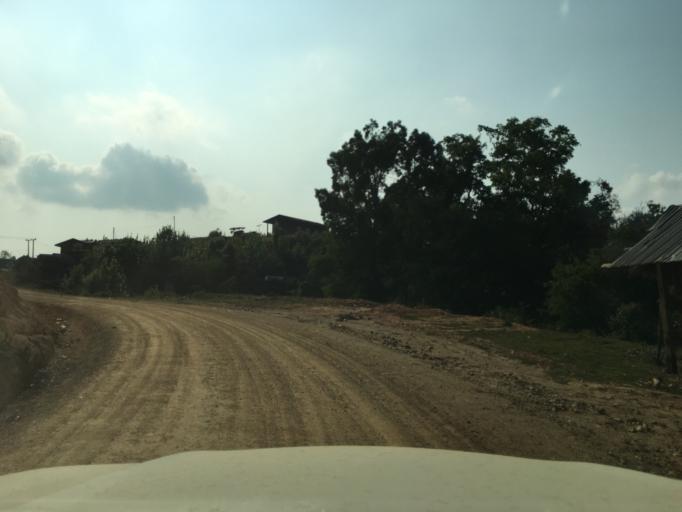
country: LA
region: Houaphan
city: Huameung
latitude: 20.1785
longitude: 103.8312
